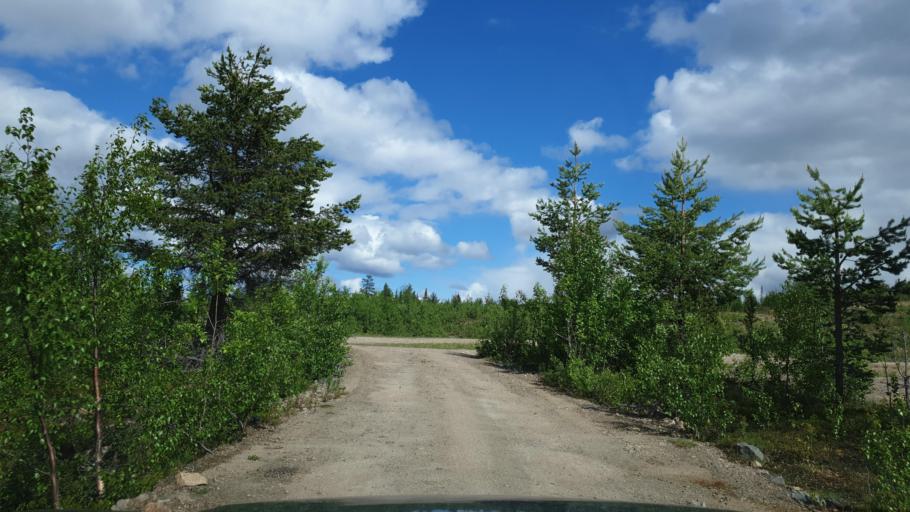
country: SE
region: Norrbotten
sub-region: Jokkmokks Kommun
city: Jokkmokk
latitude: 67.0304
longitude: 20.0038
